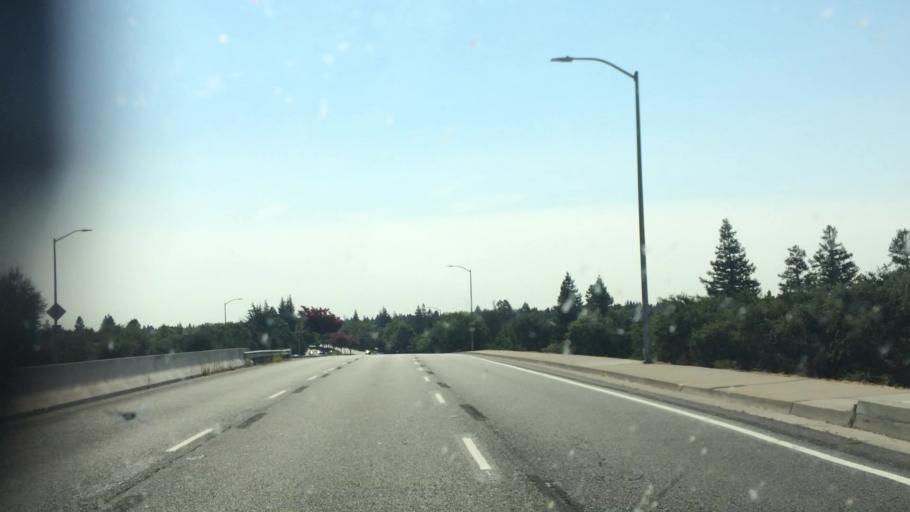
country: US
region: California
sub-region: Sacramento County
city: Laguna
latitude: 38.4237
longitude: -121.4560
